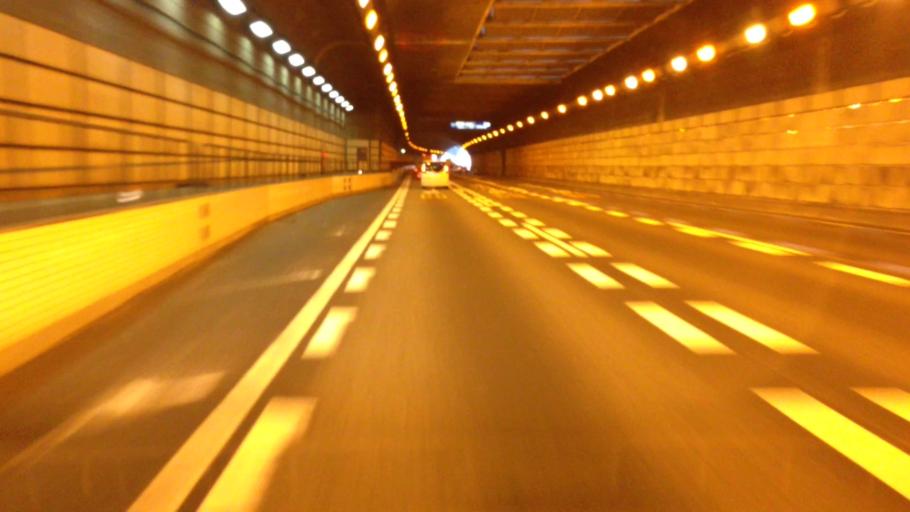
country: JP
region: Kanagawa
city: Yokohama
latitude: 35.4658
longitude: 139.5911
